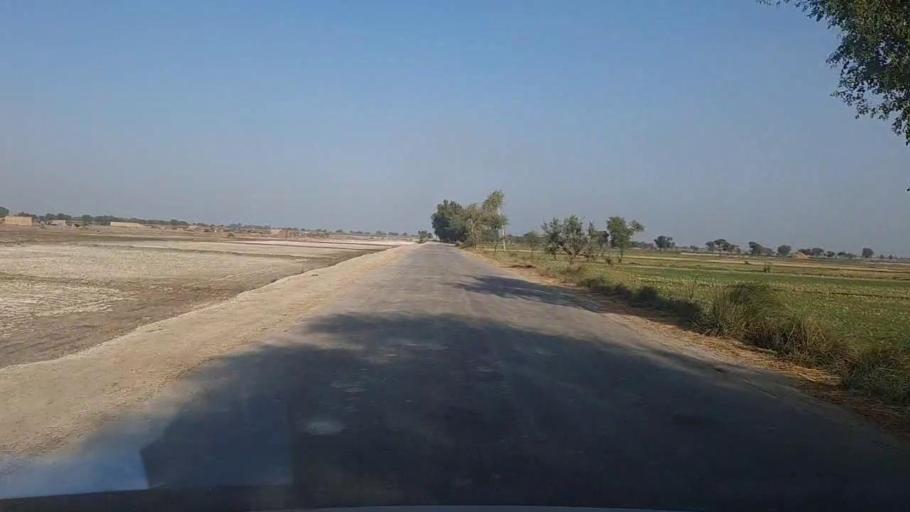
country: PK
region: Sindh
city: Dadu
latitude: 26.8426
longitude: 67.7859
